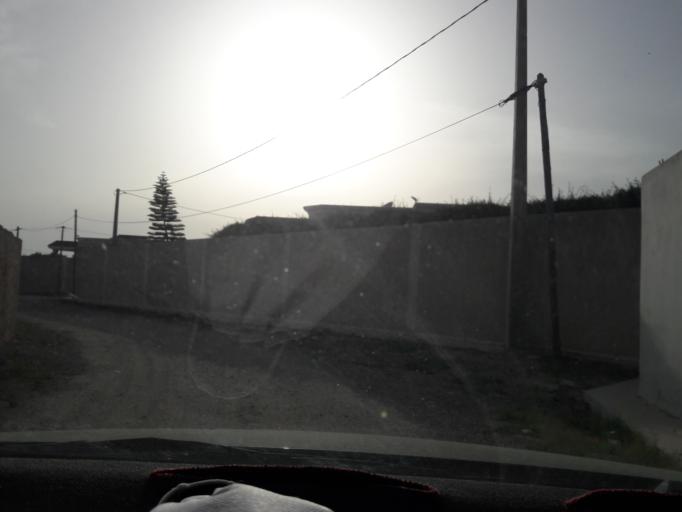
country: TN
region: Safaqis
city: Al Qarmadah
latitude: 34.8025
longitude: 10.7513
